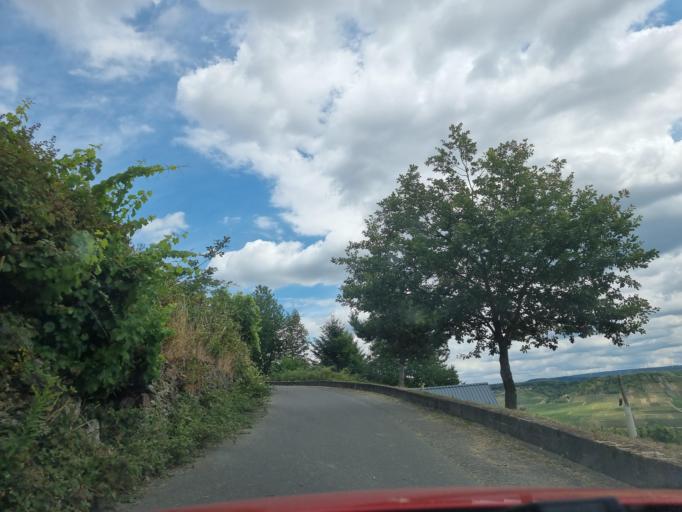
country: DE
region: Rheinland-Pfalz
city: Kesten
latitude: 49.8991
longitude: 6.9444
